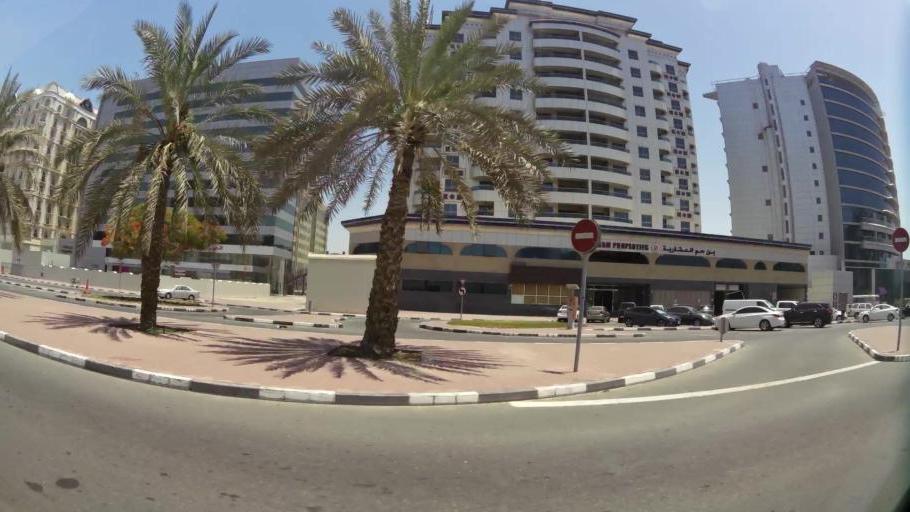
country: AE
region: Ash Shariqah
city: Sharjah
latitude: 25.2560
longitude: 55.3339
